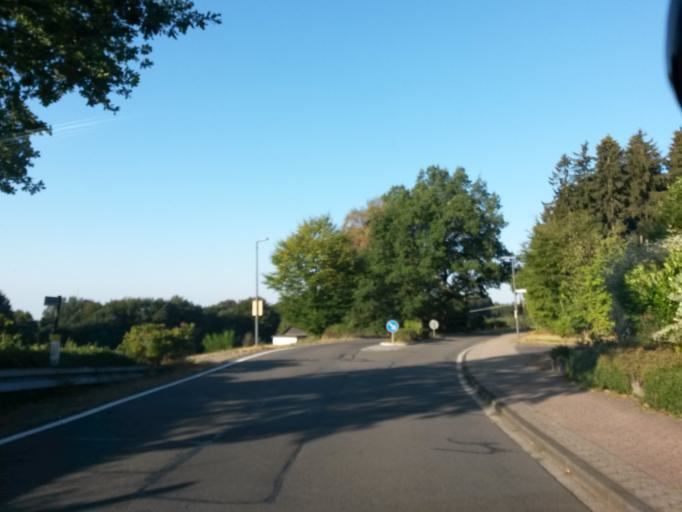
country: DE
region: North Rhine-Westphalia
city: Wipperfurth
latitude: 51.0956
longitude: 7.4191
